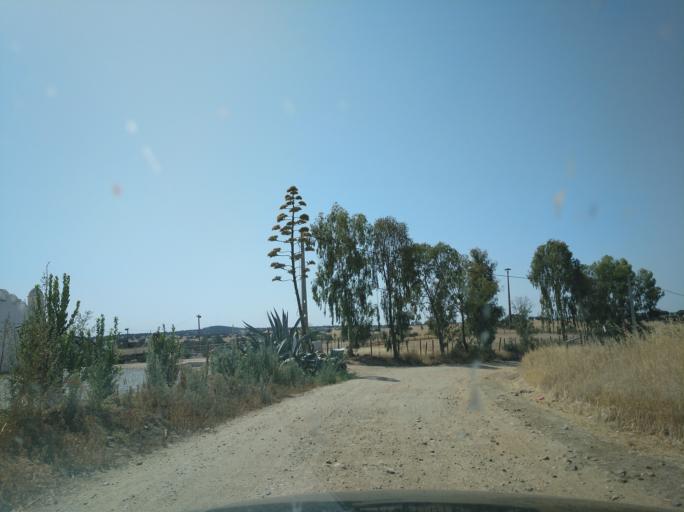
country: PT
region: Portalegre
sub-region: Campo Maior
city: Campo Maior
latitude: 39.0215
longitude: -6.9782
